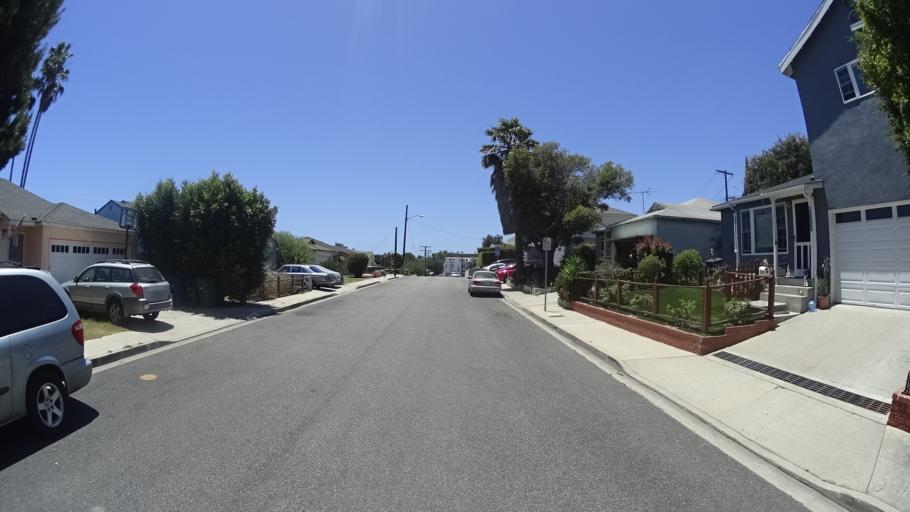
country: US
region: California
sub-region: Los Angeles County
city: Santa Monica
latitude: 34.0050
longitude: -118.4714
